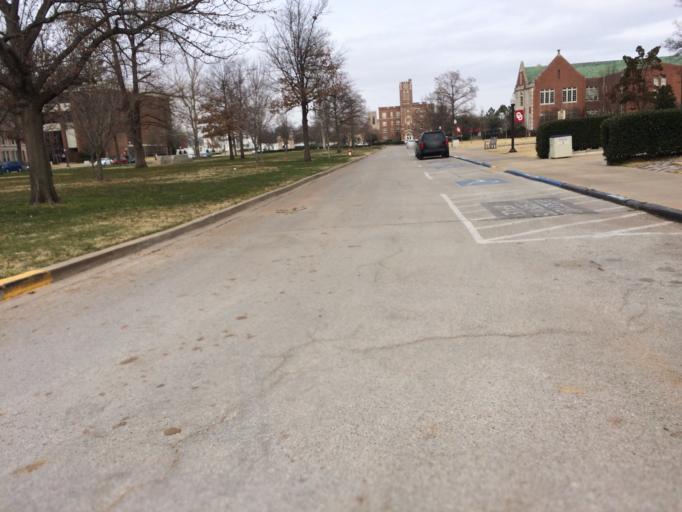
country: US
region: Oklahoma
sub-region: Cleveland County
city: Norman
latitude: 35.2092
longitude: -97.4454
